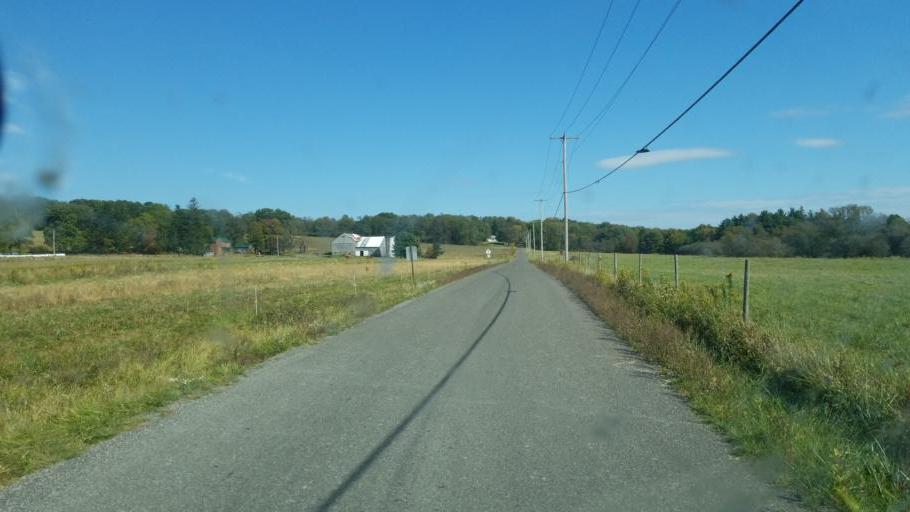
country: US
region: Pennsylvania
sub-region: Mercer County
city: Mercer
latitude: 41.3296
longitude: -80.2804
